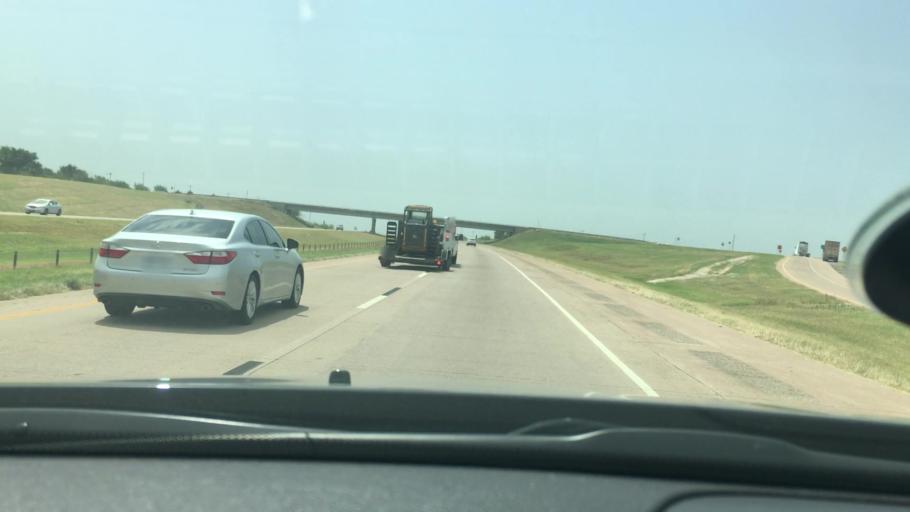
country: US
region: Oklahoma
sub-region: Garvin County
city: Pauls Valley
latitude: 34.7083
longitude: -97.2470
